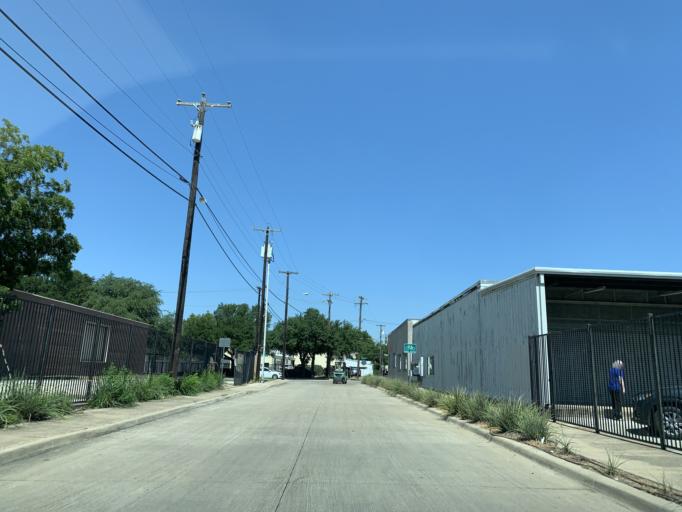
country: US
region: Texas
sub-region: Dallas County
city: Dallas
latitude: 32.7865
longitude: -96.7703
